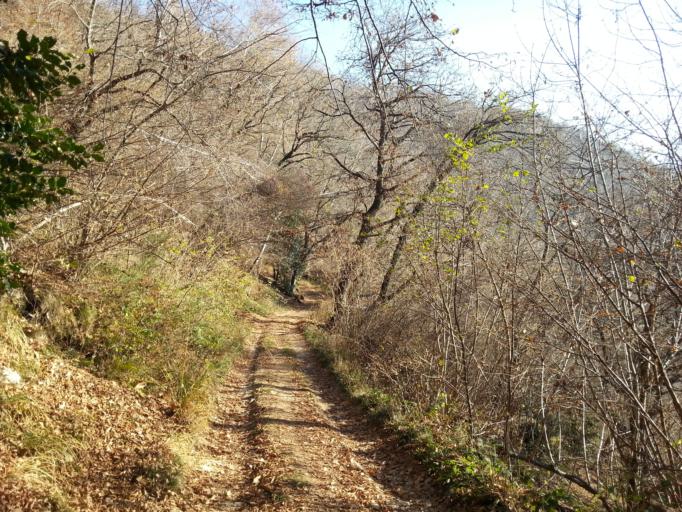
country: IT
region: Lombardy
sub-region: Provincia di Como
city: Maslianico
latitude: 45.8627
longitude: 9.0442
